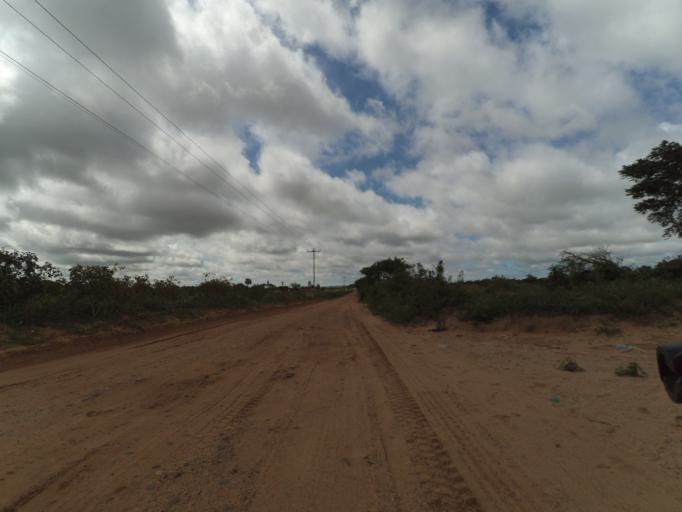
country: BO
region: Santa Cruz
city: Santa Rita
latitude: -17.9011
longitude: -63.2424
